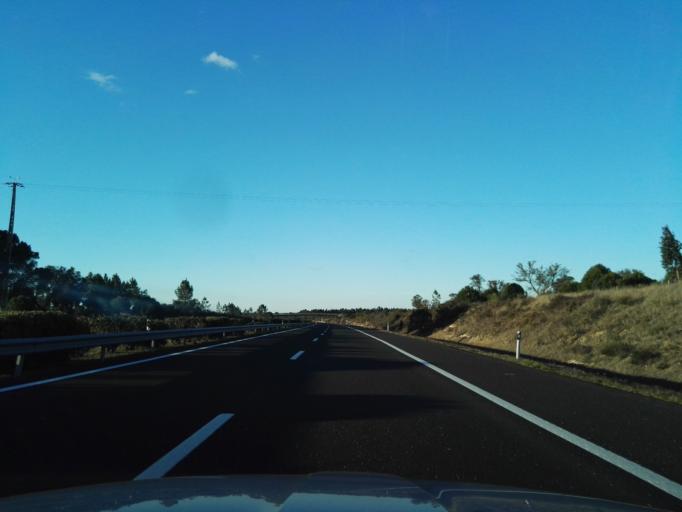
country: PT
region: Santarem
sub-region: Benavente
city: Poceirao
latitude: 38.7831
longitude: -8.6856
